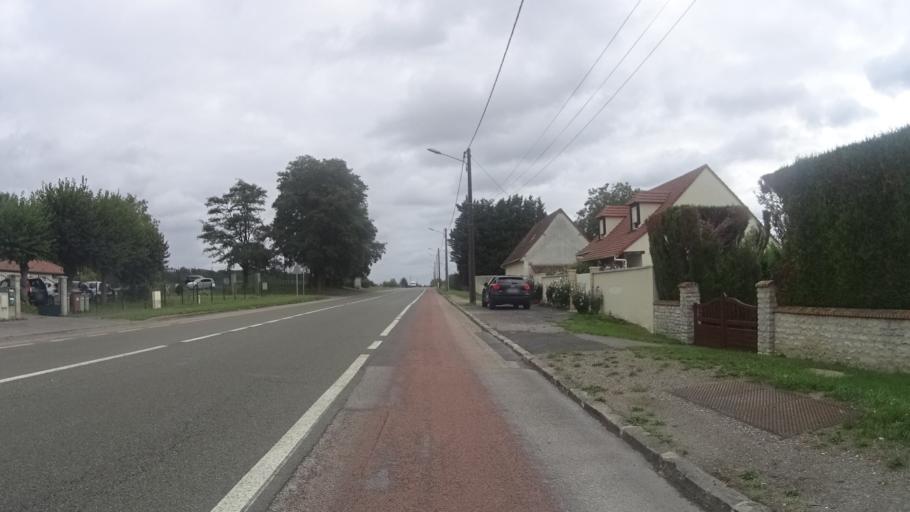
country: FR
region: Picardie
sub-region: Departement de l'Oise
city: Cambronne-les-Ribecourt
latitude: 49.5021
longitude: 2.9073
